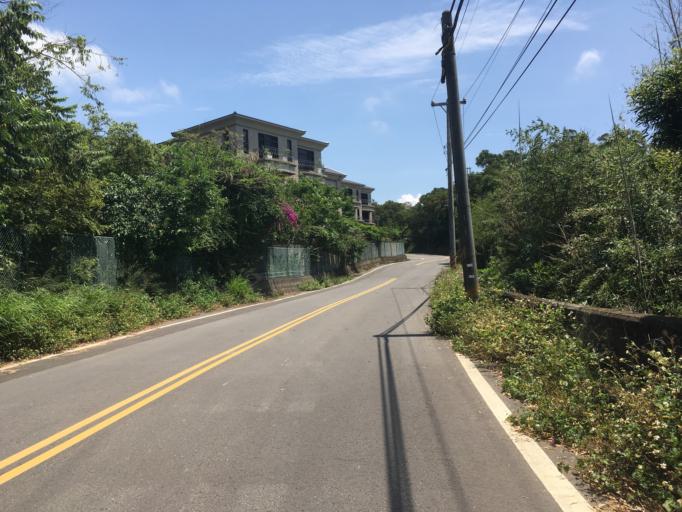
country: TW
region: Taiwan
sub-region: Hsinchu
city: Hsinchu
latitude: 24.7389
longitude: 120.9852
